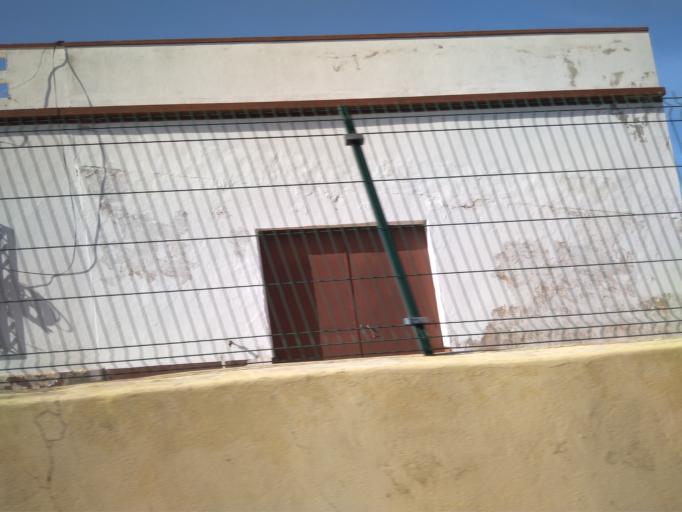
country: PT
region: Faro
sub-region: Faro
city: Santa Barbara de Nexe
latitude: 37.0633
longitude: -7.9551
